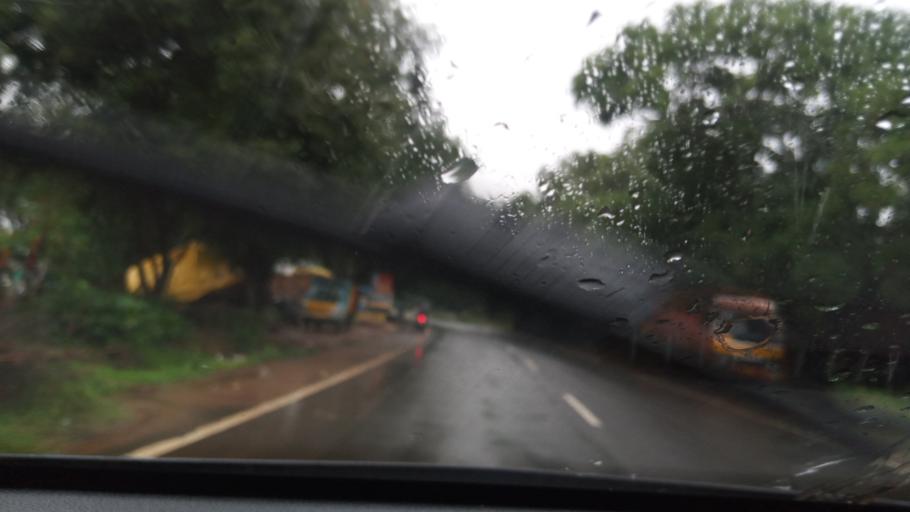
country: IN
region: Tamil Nadu
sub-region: Vellore
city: Kalavai
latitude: 12.8042
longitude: 79.4286
